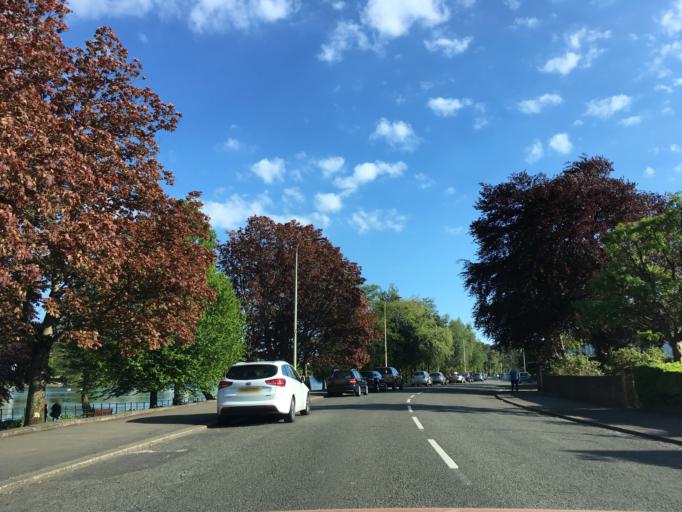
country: GB
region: Wales
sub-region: Cardiff
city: Cardiff
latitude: 51.5127
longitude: -3.1766
